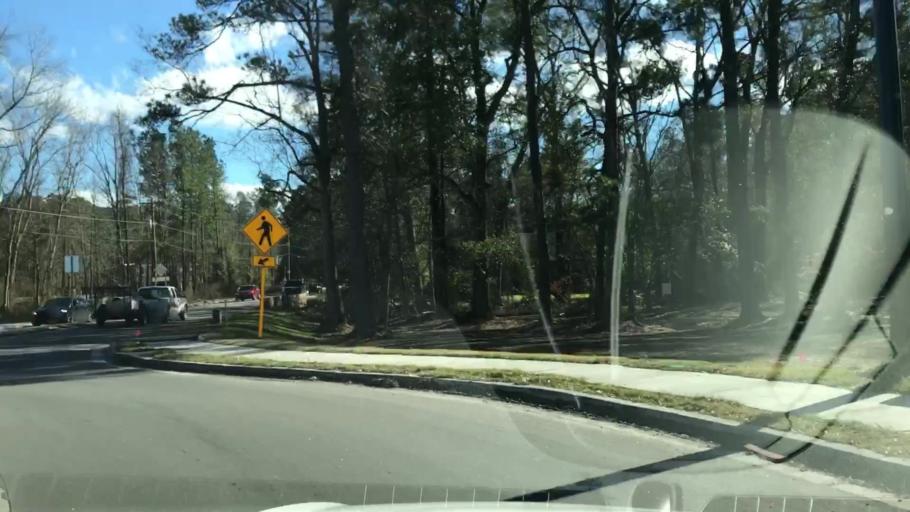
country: US
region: South Carolina
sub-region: Dorchester County
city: Summerville
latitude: 33.0223
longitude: -80.2419
